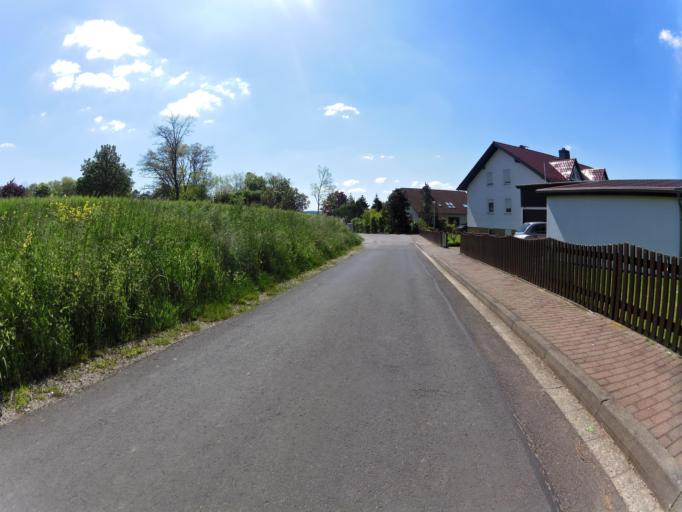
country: DE
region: Thuringia
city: Dankmarshausen
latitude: 50.9542
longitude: 10.0323
